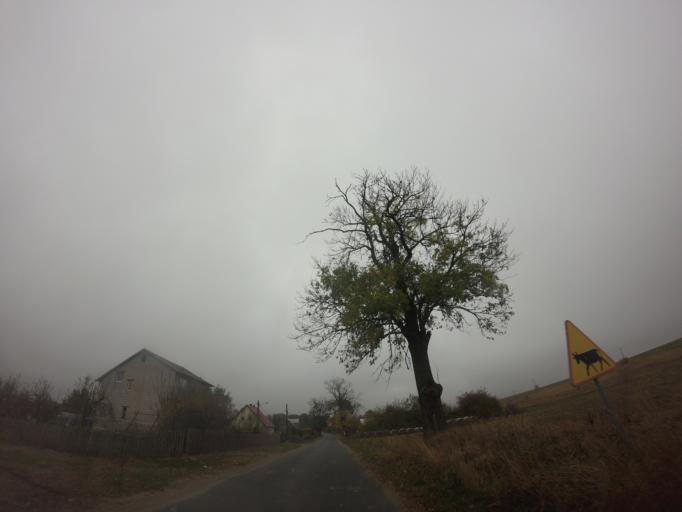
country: PL
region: West Pomeranian Voivodeship
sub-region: Powiat choszczenski
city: Choszczno
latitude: 53.1111
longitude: 15.4036
